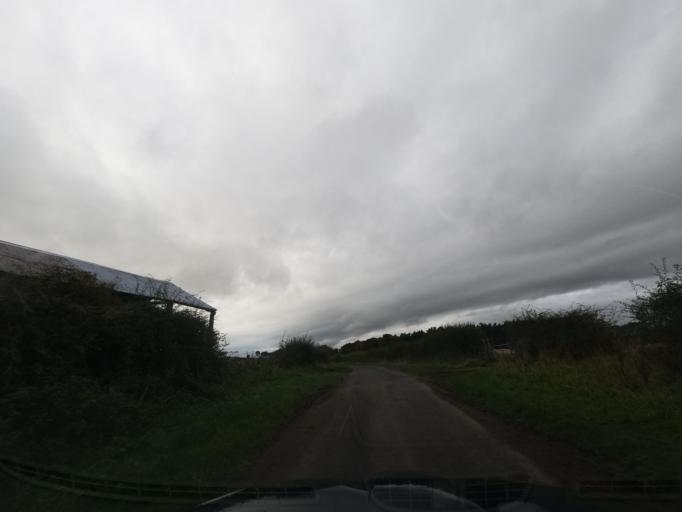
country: GB
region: England
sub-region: Northumberland
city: Doddington
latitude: 55.5946
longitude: -2.0169
